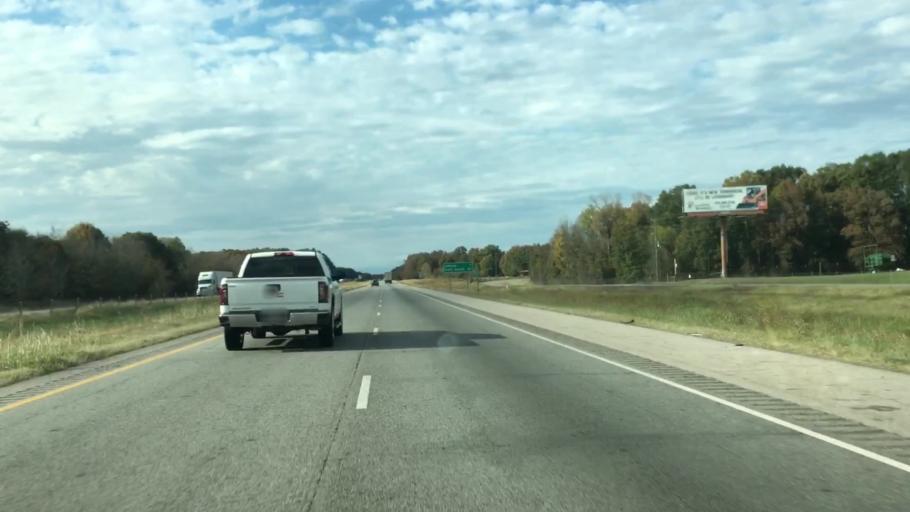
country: US
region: Arkansas
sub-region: Pope County
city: Atkins
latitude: 35.2254
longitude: -92.8379
